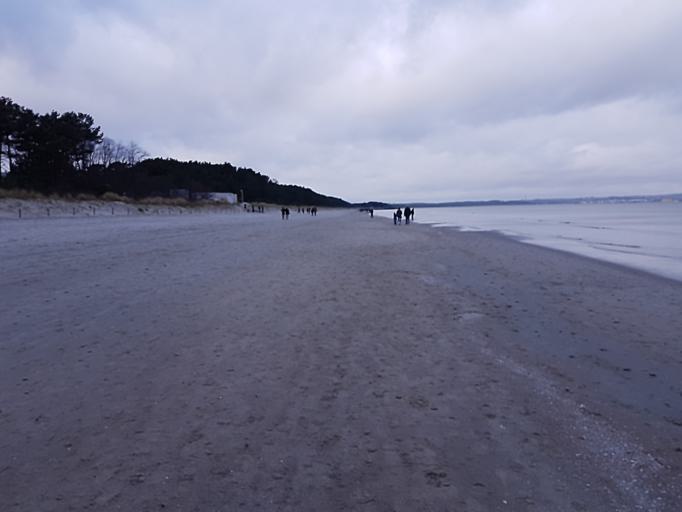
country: DE
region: Mecklenburg-Vorpommern
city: Ostseebad Binz
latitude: 54.4301
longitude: 13.5841
